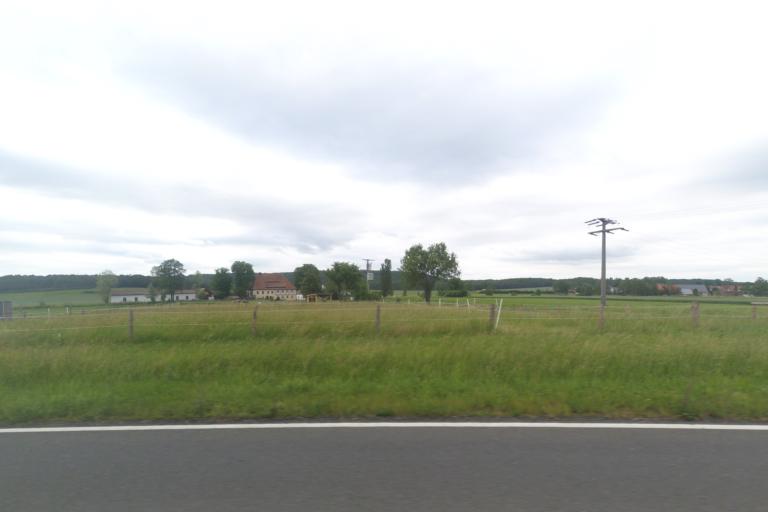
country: DE
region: Bavaria
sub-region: Regierungsbezirk Mittelfranken
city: Sugenheim
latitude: 49.6156
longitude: 10.4678
